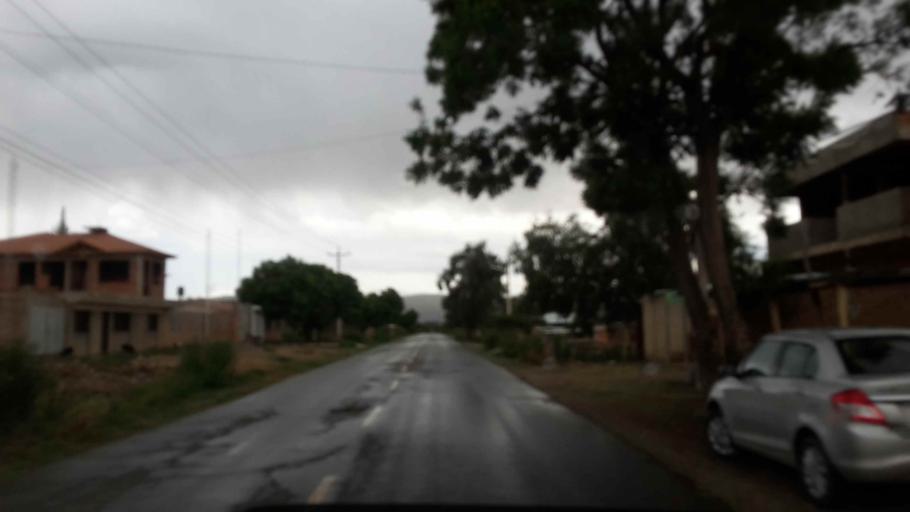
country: BO
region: Cochabamba
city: Tarata
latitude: -17.5764
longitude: -66.0608
